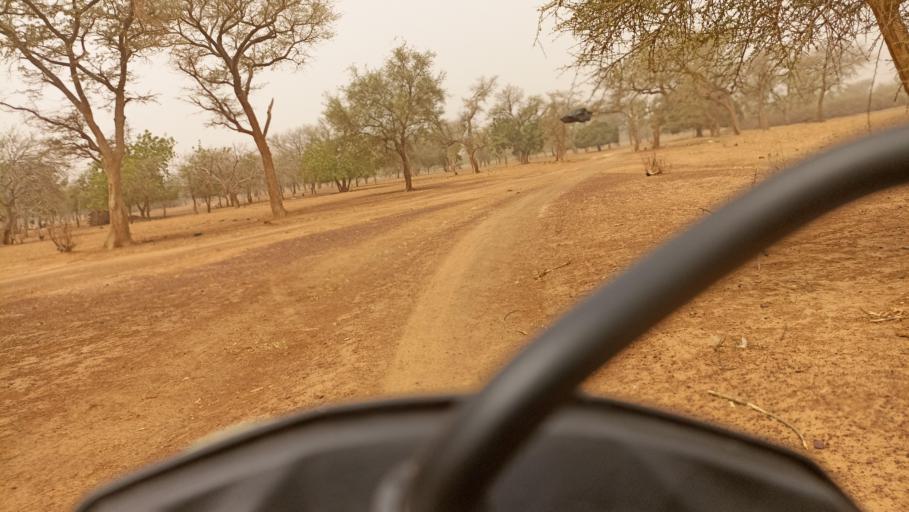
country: BF
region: Nord
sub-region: Province du Zondoma
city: Gourcy
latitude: 13.2486
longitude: -2.5952
